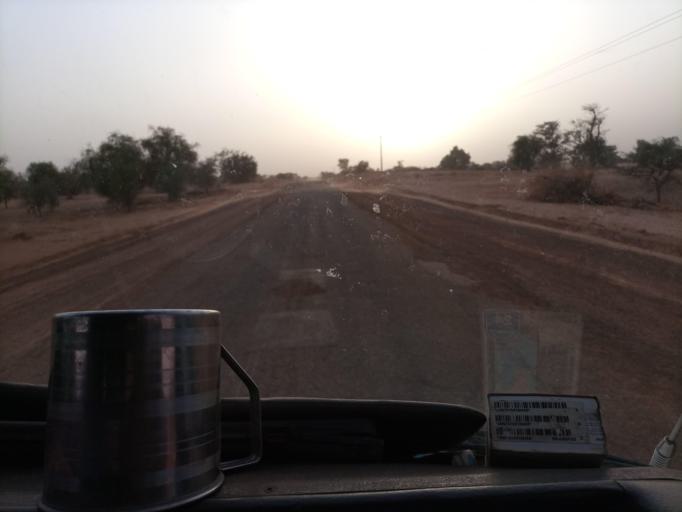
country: SN
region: Louga
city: Dara
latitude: 15.4063
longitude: -15.6688
